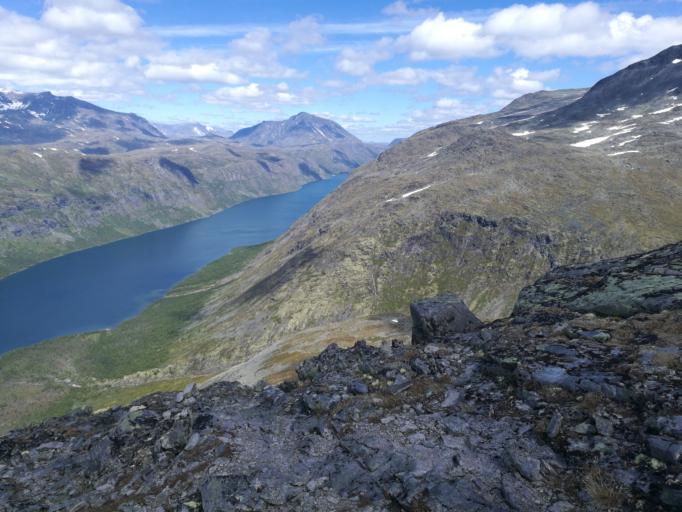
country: NO
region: Oppland
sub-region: Vang
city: Vang
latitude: 61.4350
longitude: 8.4935
